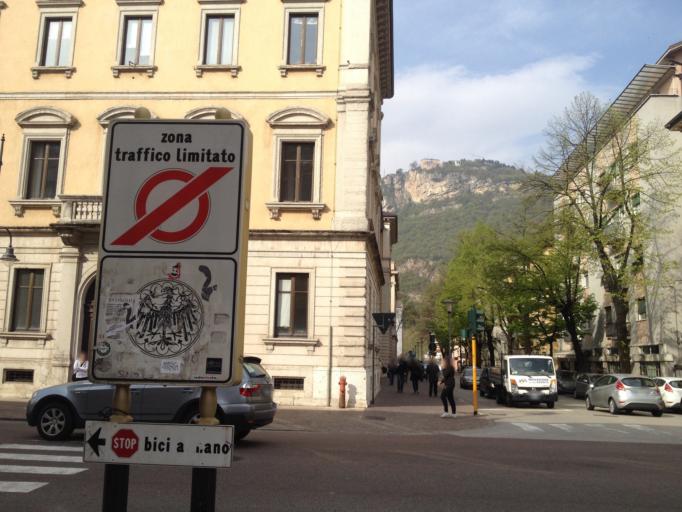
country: IT
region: Trentino-Alto Adige
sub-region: Provincia di Trento
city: Trento
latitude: 46.0667
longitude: 11.1192
